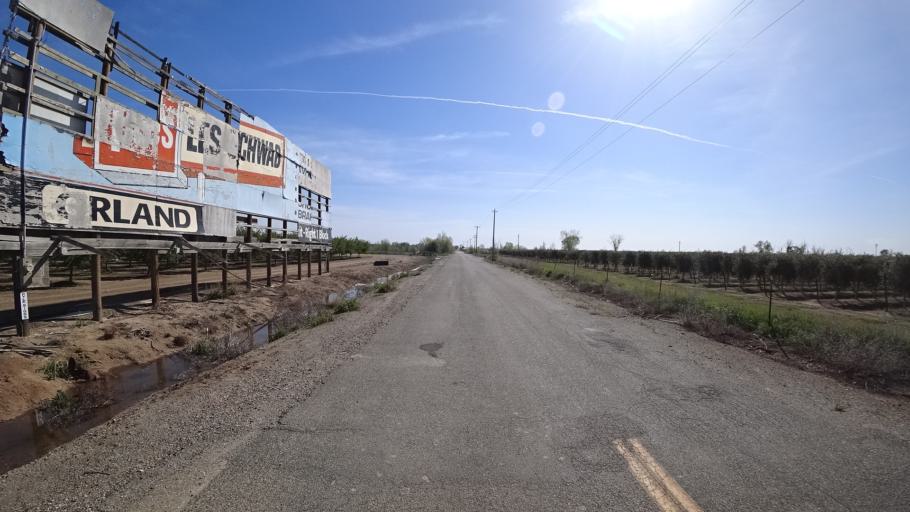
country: US
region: California
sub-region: Glenn County
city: Willows
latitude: 39.6114
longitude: -122.2046
